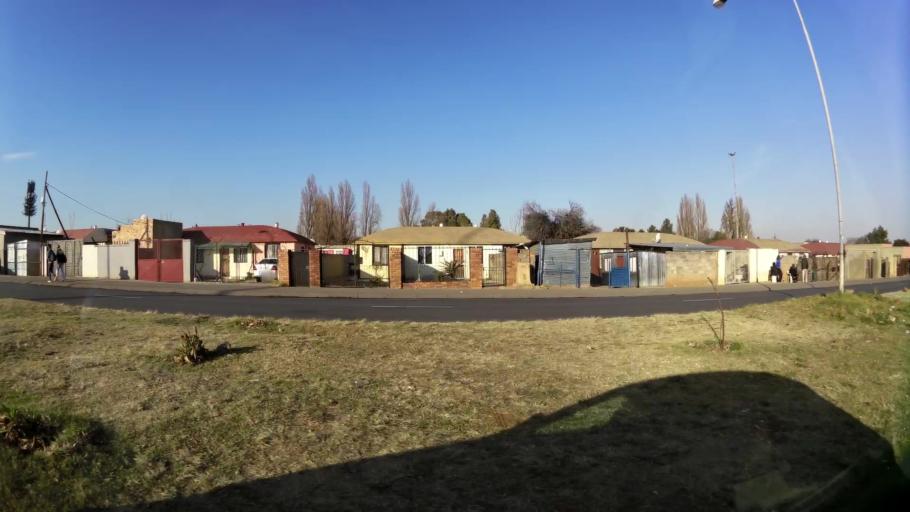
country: ZA
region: Gauteng
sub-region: City of Johannesburg Metropolitan Municipality
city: Soweto
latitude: -26.2535
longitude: 27.8777
